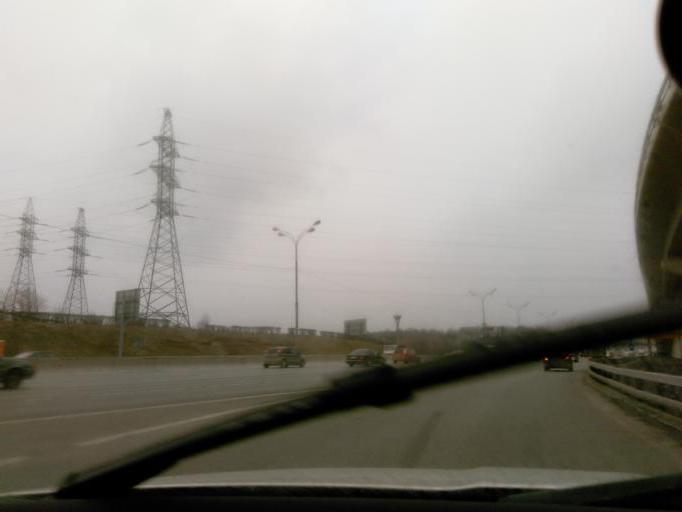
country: RU
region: Moscow
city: Khimki
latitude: 55.8810
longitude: 37.4413
